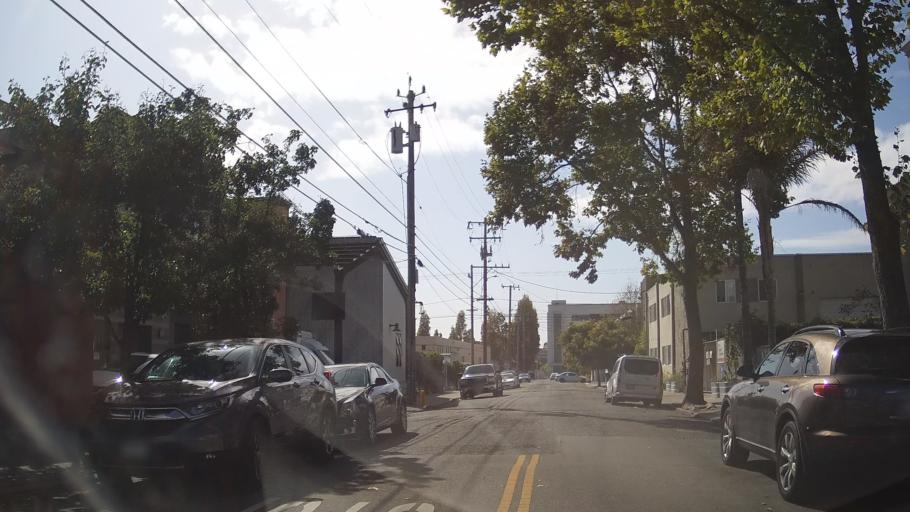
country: US
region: California
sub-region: Alameda County
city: Berkeley
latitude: 37.8566
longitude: -122.2907
